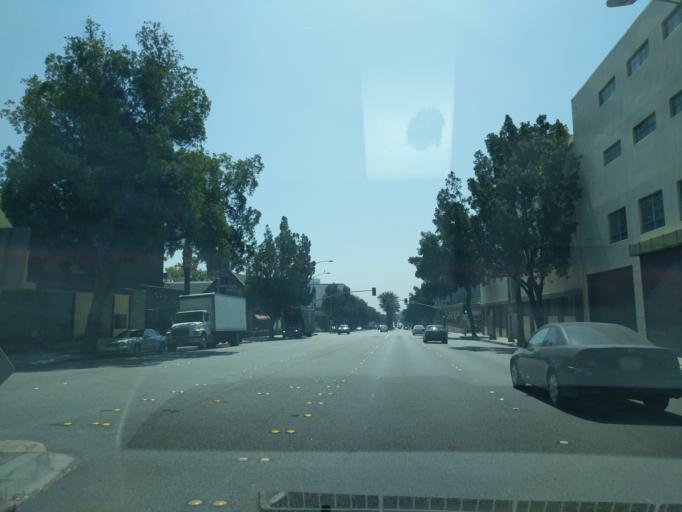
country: US
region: California
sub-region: Los Angeles County
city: Pasadena
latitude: 34.1392
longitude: -118.1474
